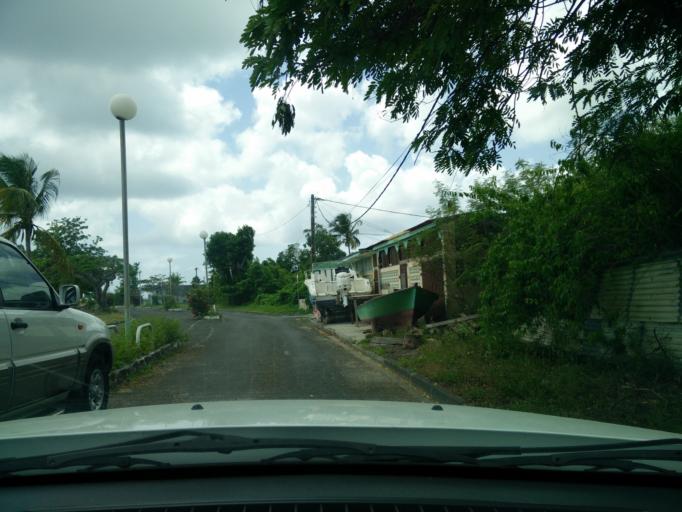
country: GP
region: Guadeloupe
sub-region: Guadeloupe
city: Port-Louis
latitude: 16.4138
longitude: -61.5324
